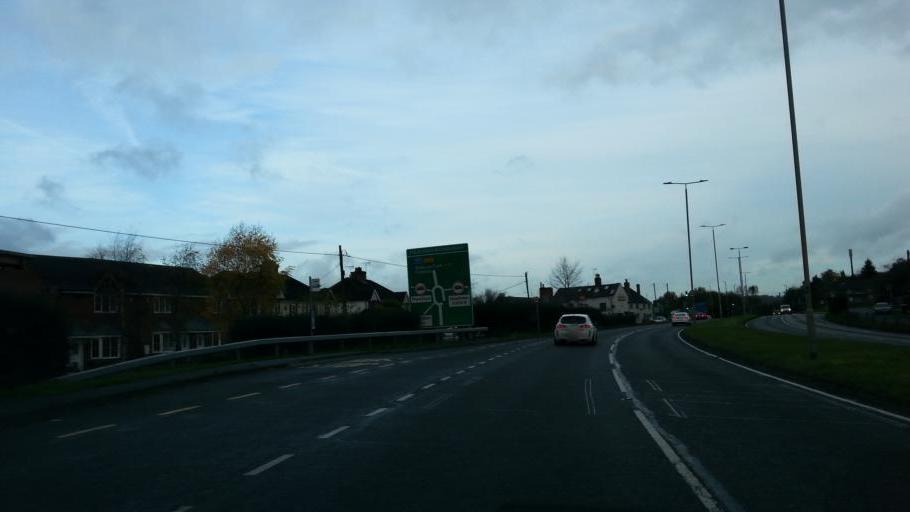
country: GB
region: England
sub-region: Leicestershire
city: Markfield
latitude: 52.6843
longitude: -1.2662
